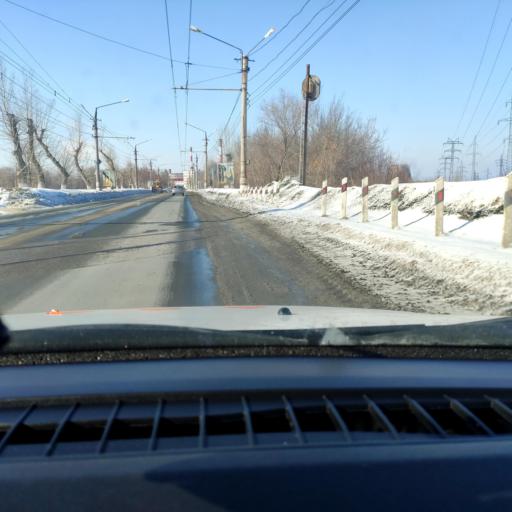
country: RU
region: Samara
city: Novokuybyshevsk
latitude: 53.1044
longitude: 49.9346
